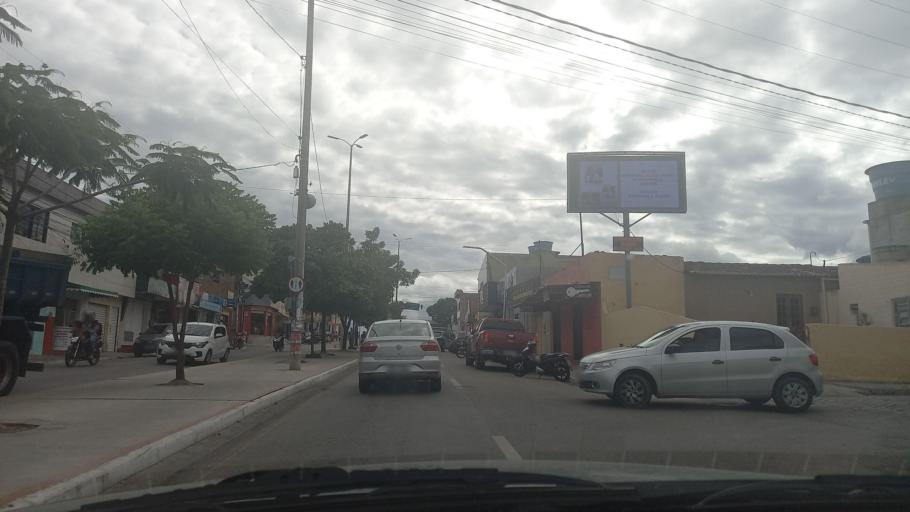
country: BR
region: Pernambuco
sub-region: Caruaru
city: Caruaru
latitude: -8.2746
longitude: -35.9903
